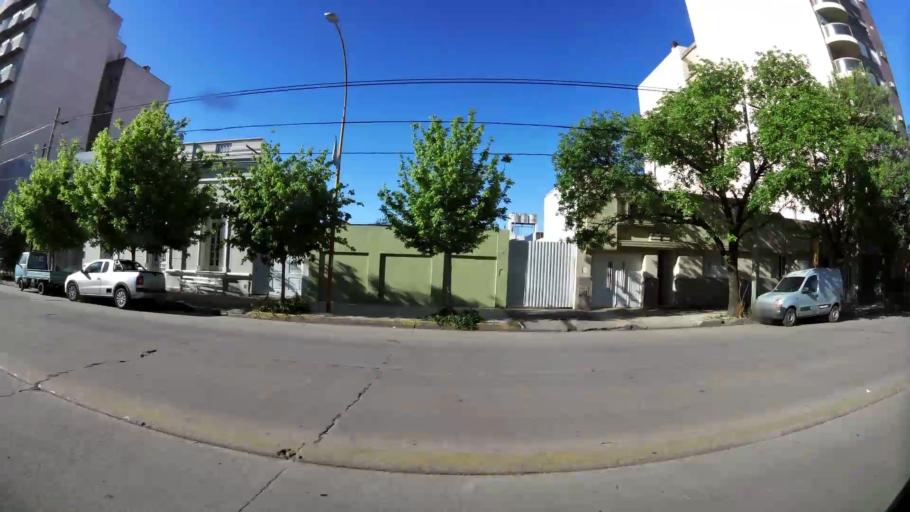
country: AR
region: Cordoba
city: San Francisco
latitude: -31.4295
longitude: -62.0936
